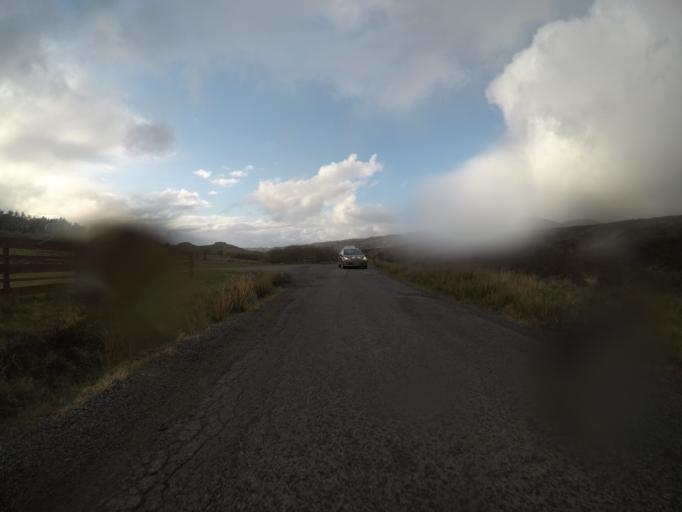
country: GB
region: Scotland
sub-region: Highland
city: Isle of Skye
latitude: 57.4671
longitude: -6.2986
